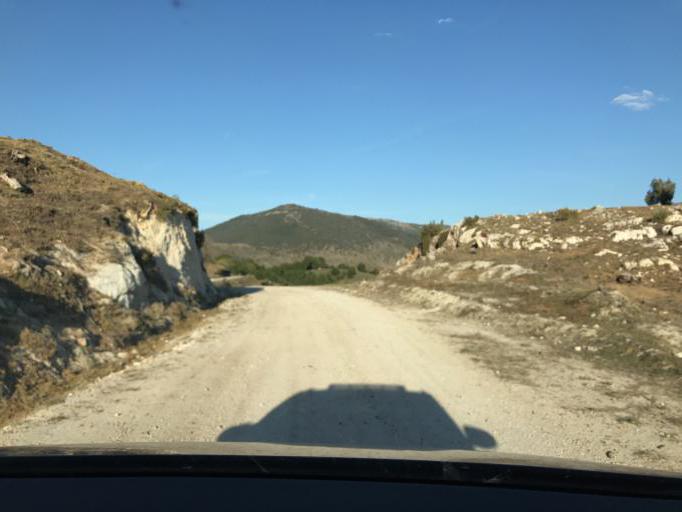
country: ES
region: Andalusia
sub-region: Provincia de Granada
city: Quentar
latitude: 37.2389
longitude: -3.3937
